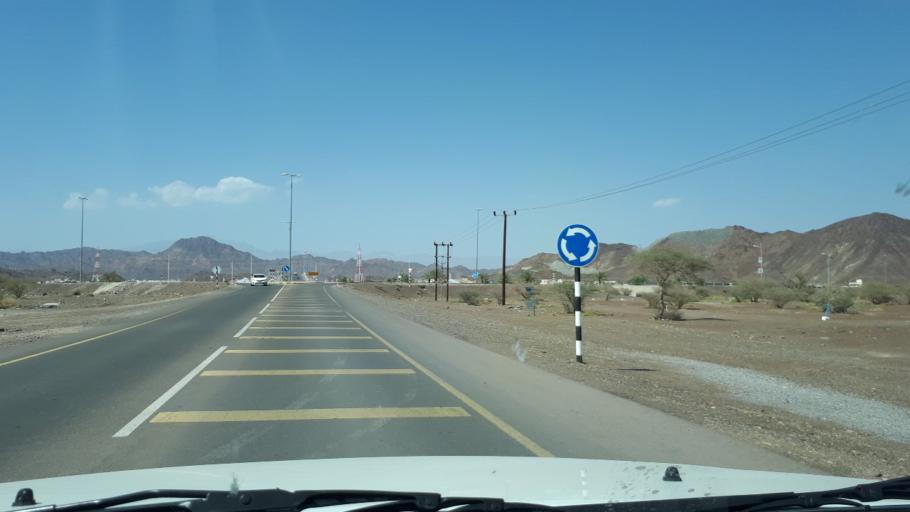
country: OM
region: Muhafazat ad Dakhiliyah
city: Bahla'
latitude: 22.9235
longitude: 57.2559
